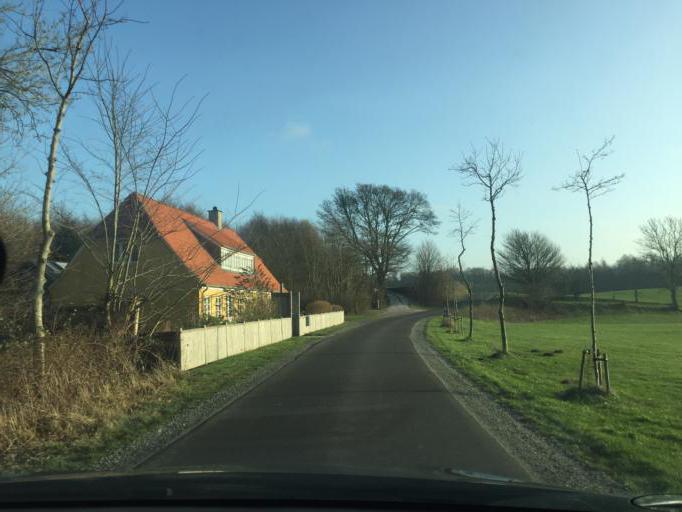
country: DK
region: South Denmark
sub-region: Faaborg-Midtfyn Kommune
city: Faaborg
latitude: 55.1364
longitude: 10.2526
